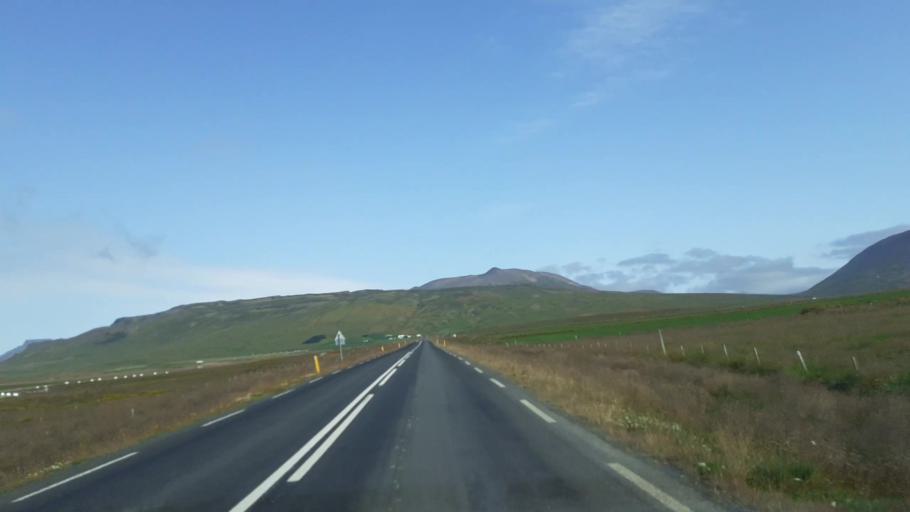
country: IS
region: Northwest
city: Saudarkrokur
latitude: 65.7113
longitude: -20.2278
